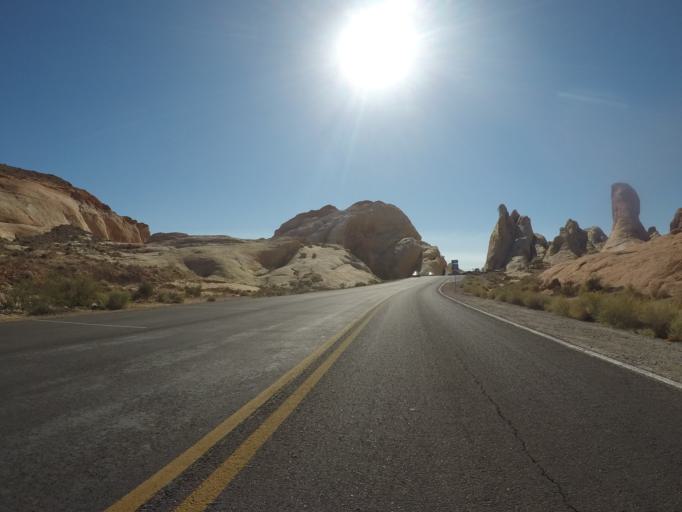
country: US
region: Nevada
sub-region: Clark County
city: Moapa Valley
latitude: 36.4876
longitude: -114.5331
